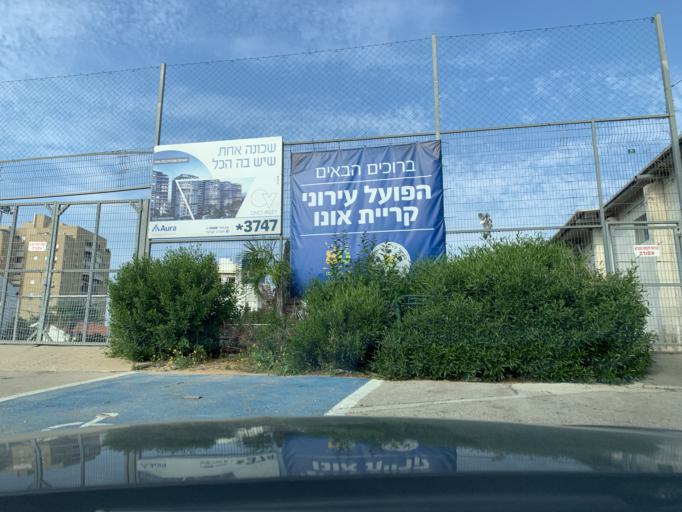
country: IL
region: Tel Aviv
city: Giv`at Shemu'el
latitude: 32.0631
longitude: 34.8494
